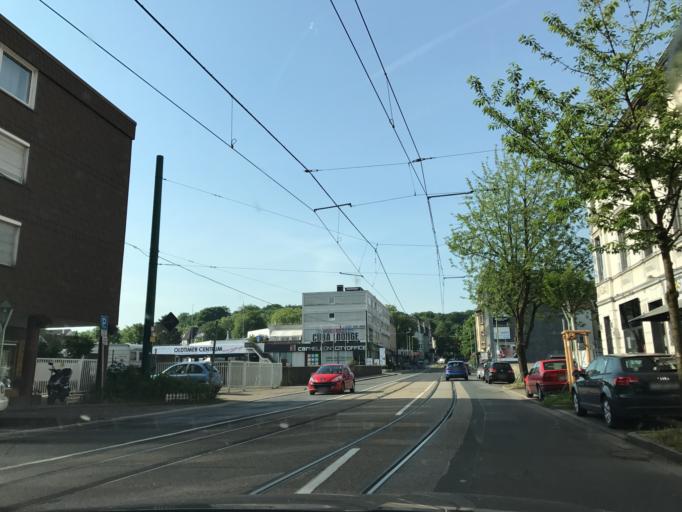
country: DE
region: North Rhine-Westphalia
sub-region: Regierungsbezirk Dusseldorf
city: Essen
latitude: 51.4237
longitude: 7.0016
